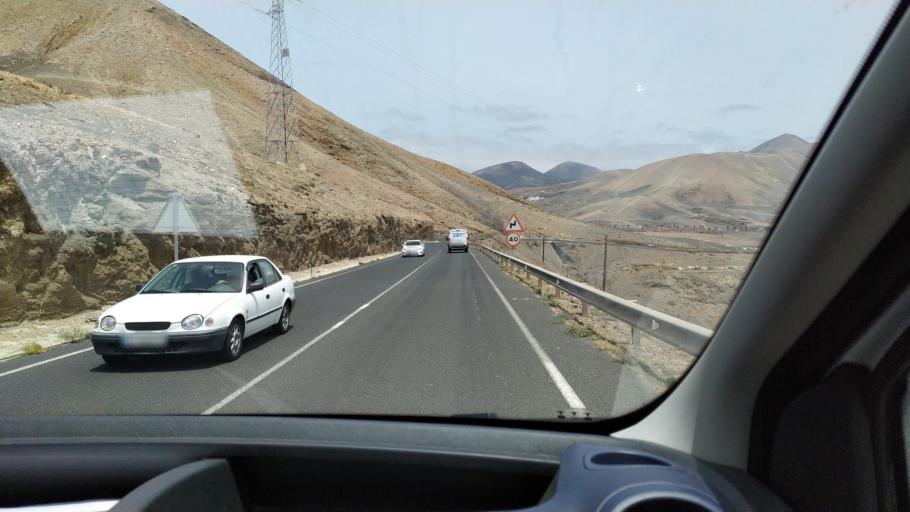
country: ES
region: Canary Islands
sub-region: Provincia de Las Palmas
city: Yaiza
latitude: 28.9315
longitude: -13.7481
